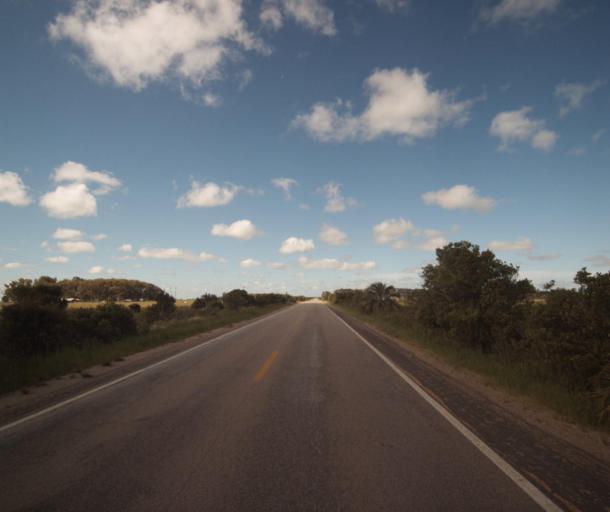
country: BR
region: Rio Grande do Sul
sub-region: Santa Vitoria Do Palmar
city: Santa Vitoria do Palmar
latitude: -33.4143
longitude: -53.2327
